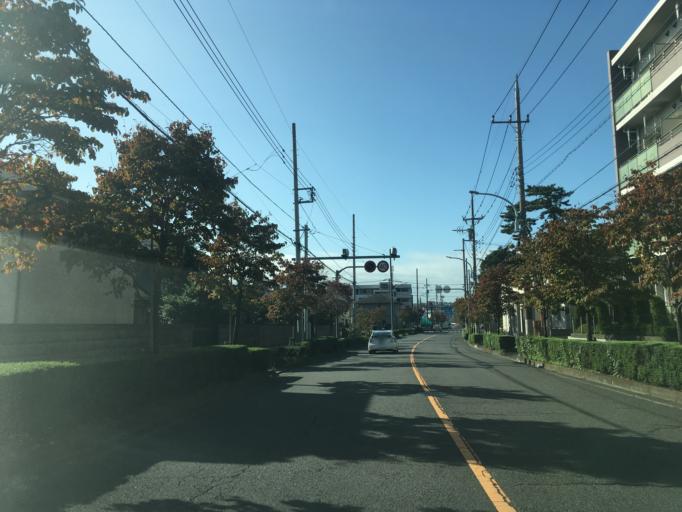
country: JP
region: Tokyo
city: Hino
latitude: 35.6724
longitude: 139.4093
